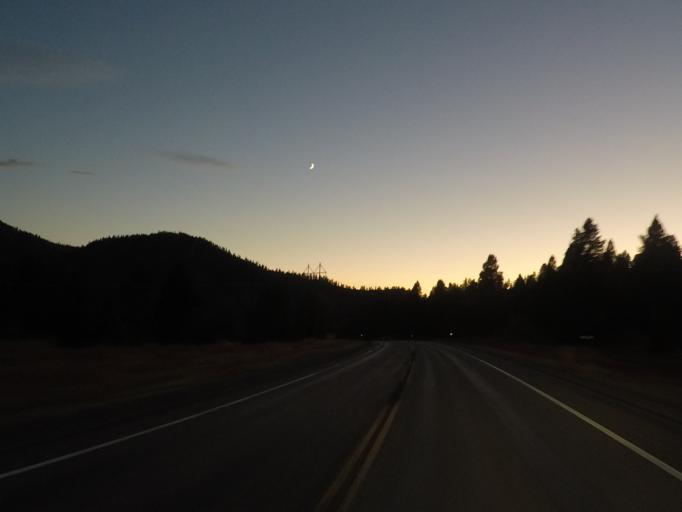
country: US
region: Montana
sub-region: Missoula County
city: Seeley Lake
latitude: 47.0284
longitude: -113.2843
